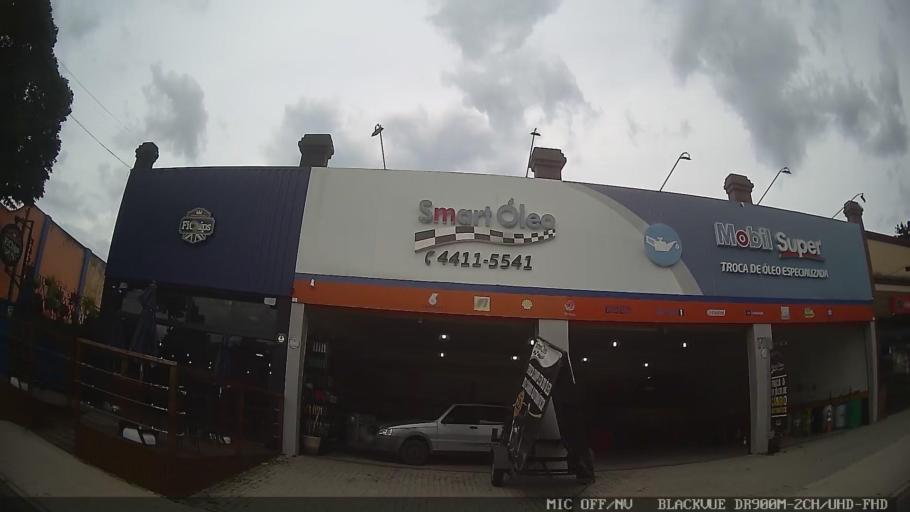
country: BR
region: Sao Paulo
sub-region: Atibaia
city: Atibaia
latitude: -23.1239
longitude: -46.5536
